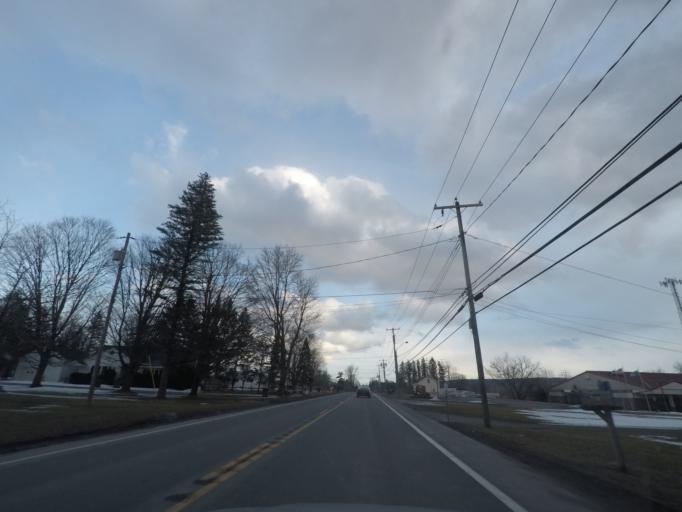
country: US
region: New York
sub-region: Oneida County
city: Utica
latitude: 43.1050
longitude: -75.1637
